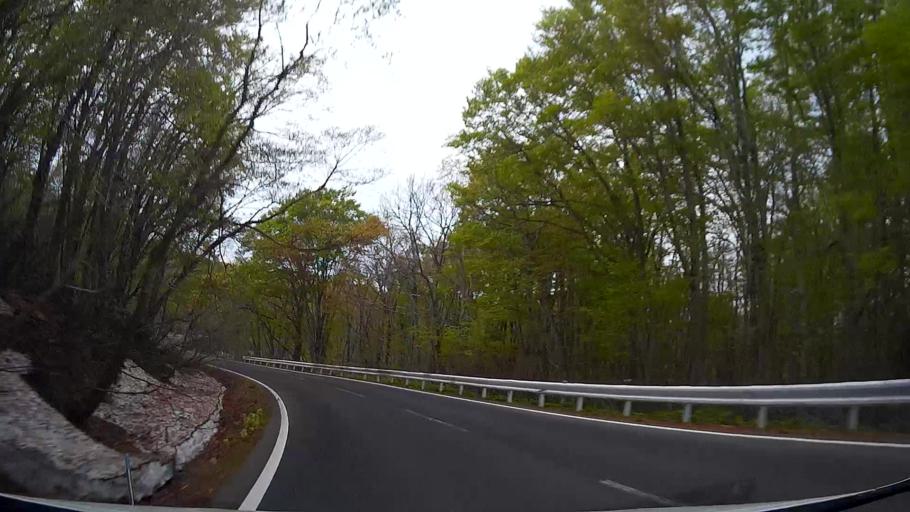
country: JP
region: Aomori
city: Aomori Shi
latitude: 40.7025
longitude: 140.8287
